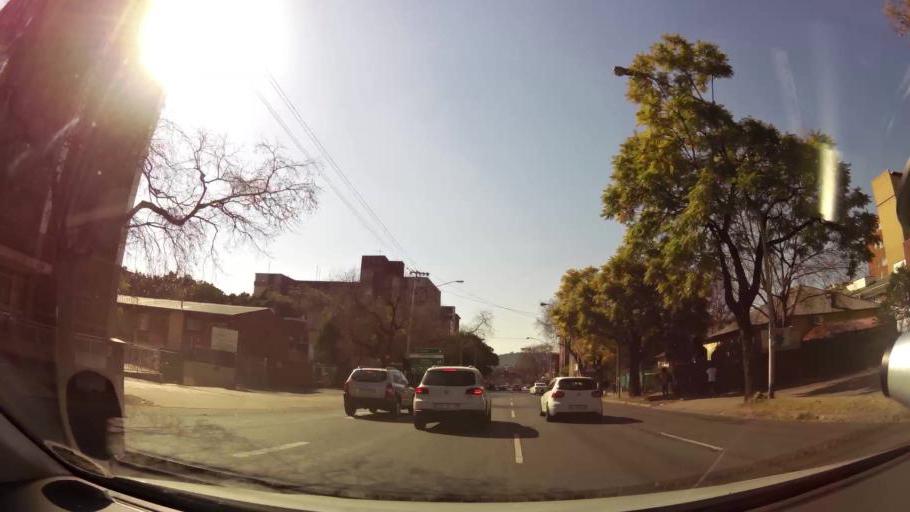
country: ZA
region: Gauteng
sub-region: City of Tshwane Metropolitan Municipality
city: Pretoria
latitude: -25.7545
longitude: 28.2020
